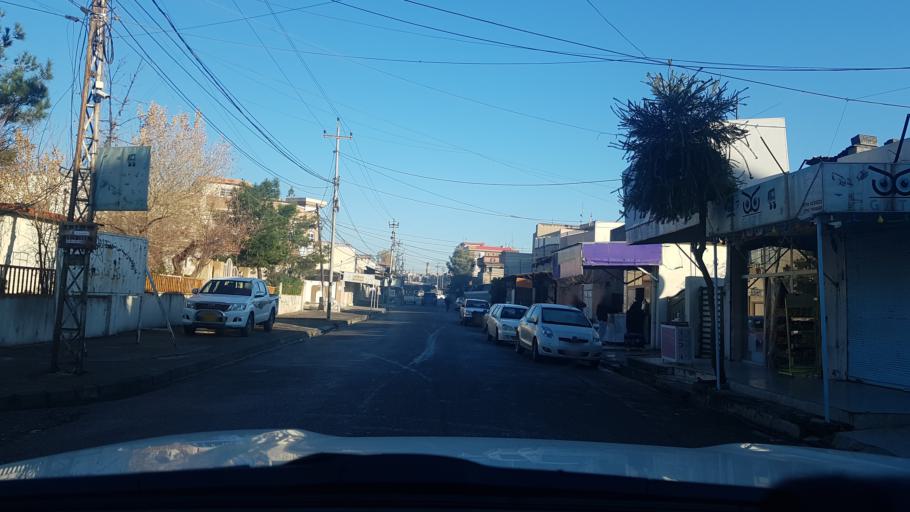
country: IQ
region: Arbil
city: Erbil
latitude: 36.2050
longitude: 44.0086
